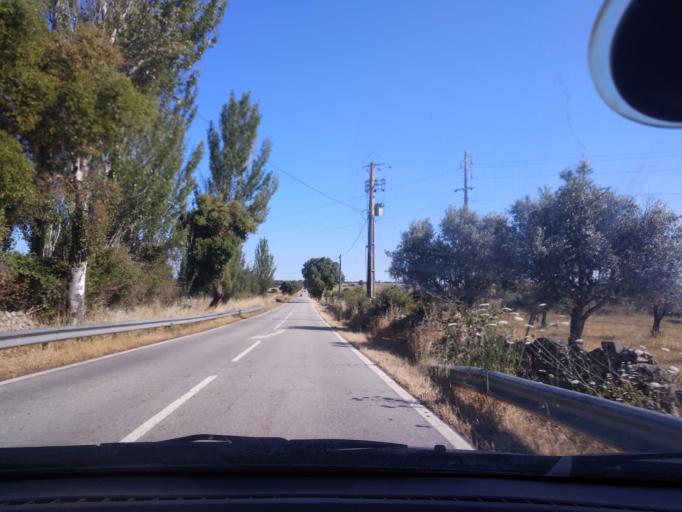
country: PT
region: Portalegre
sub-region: Nisa
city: Nisa
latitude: 39.4287
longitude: -7.6219
